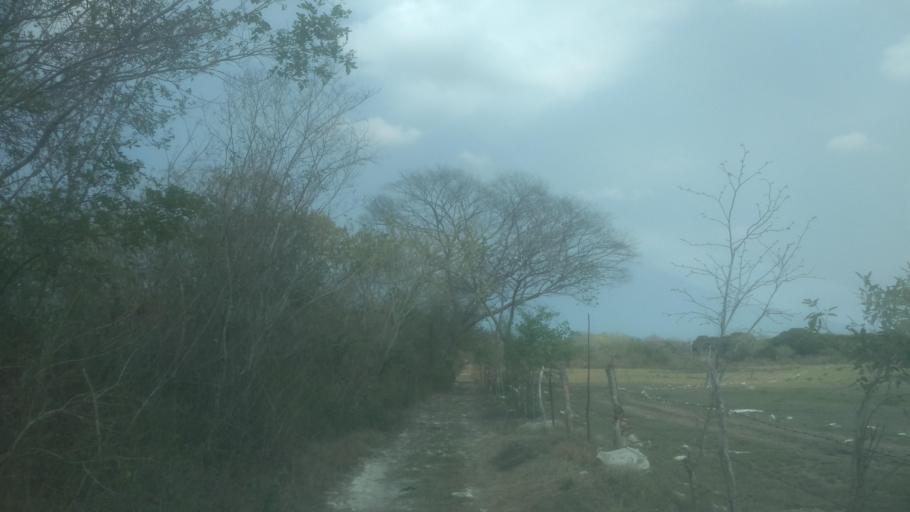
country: MX
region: Veracruz
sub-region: Emiliano Zapata
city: Plan del Rio
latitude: 19.3872
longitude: -96.6272
